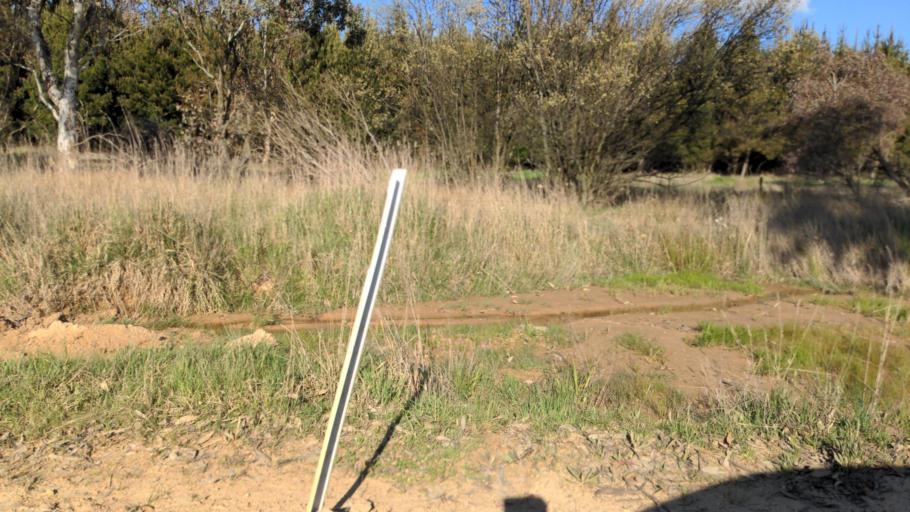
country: AU
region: New South Wales
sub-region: Blayney
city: Millthorpe
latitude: -33.3981
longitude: 149.3090
